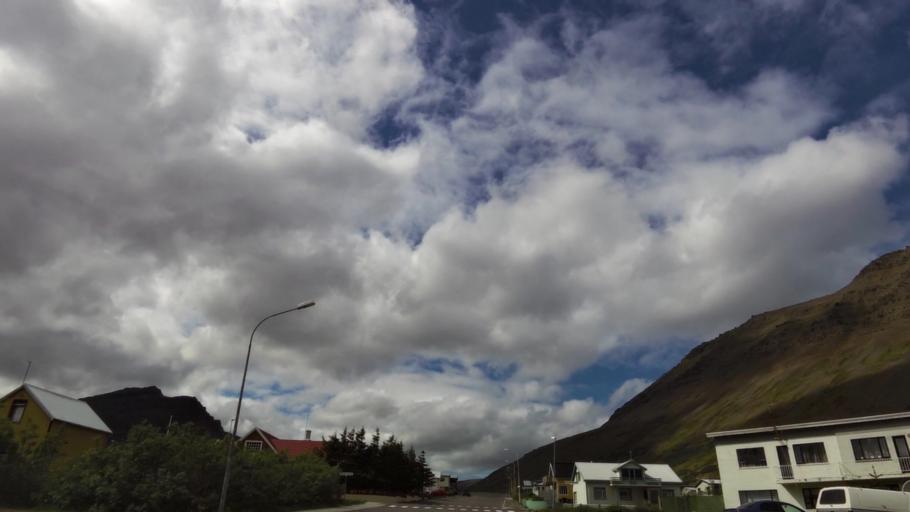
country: IS
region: Westfjords
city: Isafjoerdur
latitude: 66.1574
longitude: -23.2544
